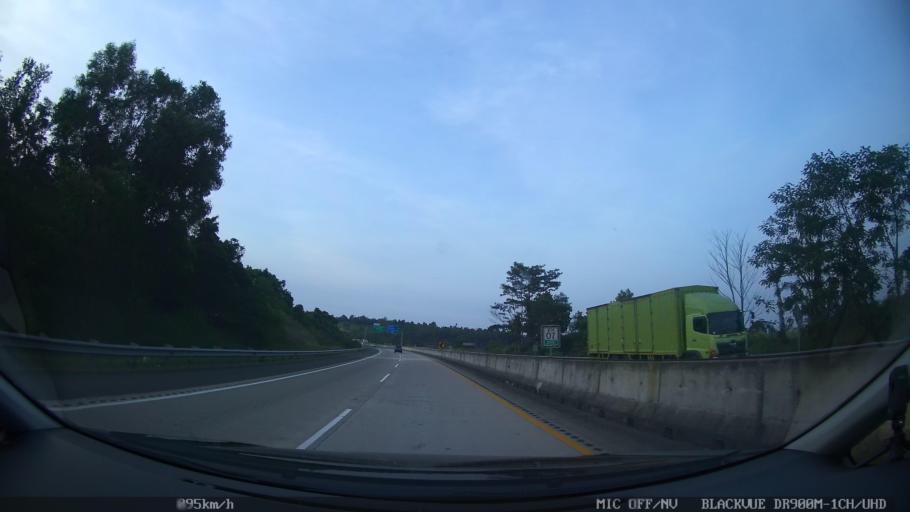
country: ID
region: Lampung
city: Penengahan
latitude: -5.8207
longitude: 105.7382
